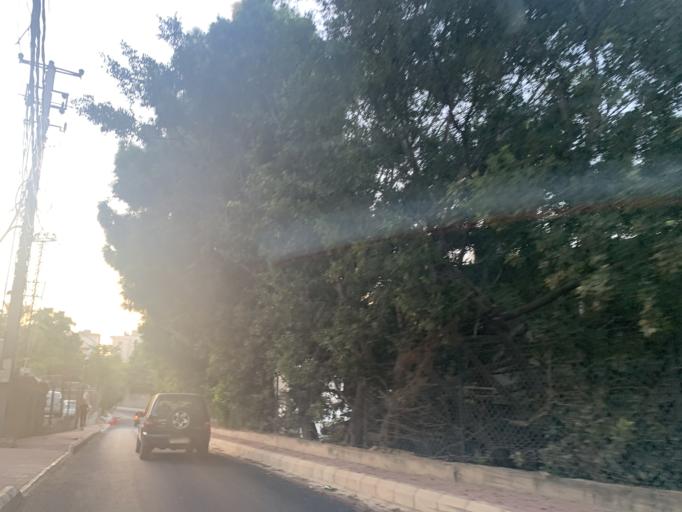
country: LB
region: Mont-Liban
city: Djounie
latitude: 33.9739
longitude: 35.6285
